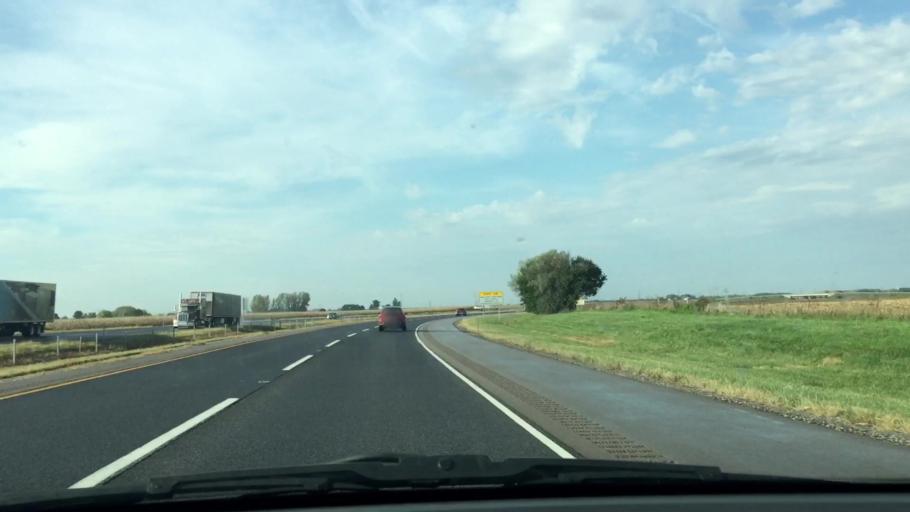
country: US
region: Illinois
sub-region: Lee County
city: Dixon
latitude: 41.7842
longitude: -89.5394
